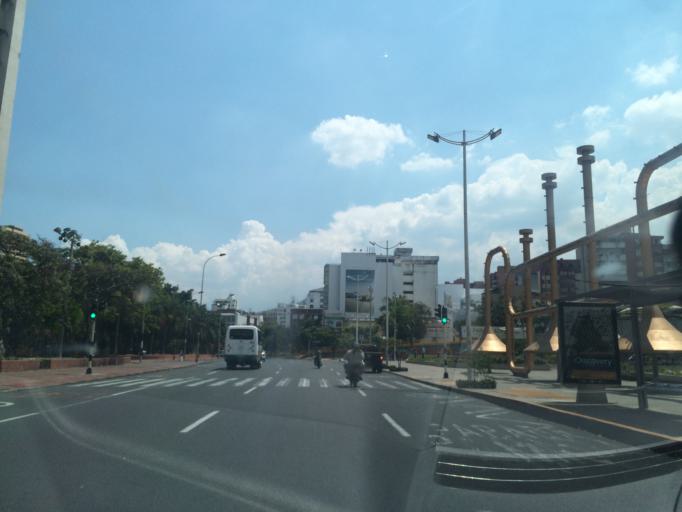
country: CO
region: Valle del Cauca
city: Cali
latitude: 3.4550
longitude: -76.5344
